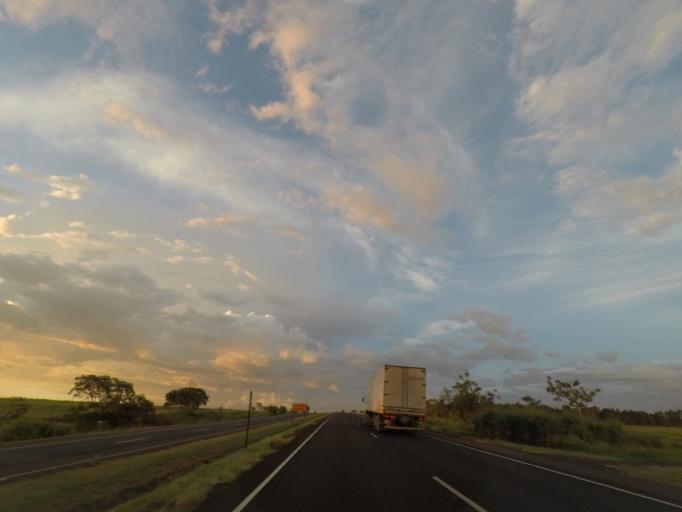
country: BR
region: Minas Gerais
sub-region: Uberaba
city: Uberaba
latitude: -19.6434
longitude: -48.0086
